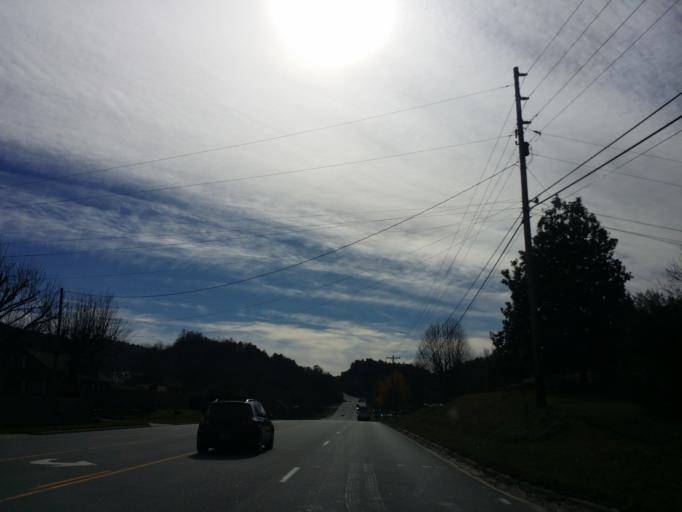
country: US
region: North Carolina
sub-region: McDowell County
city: Marion
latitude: 35.7894
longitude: -82.0390
